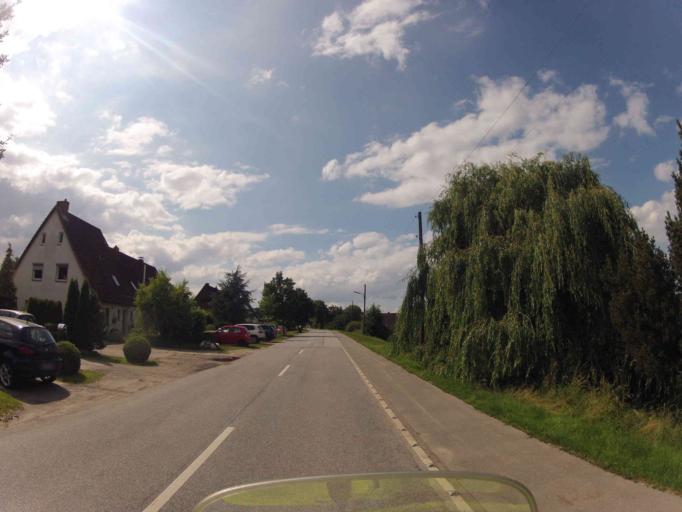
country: DE
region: Hamburg
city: Rothenburgsort
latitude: 53.4997
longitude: 10.0849
